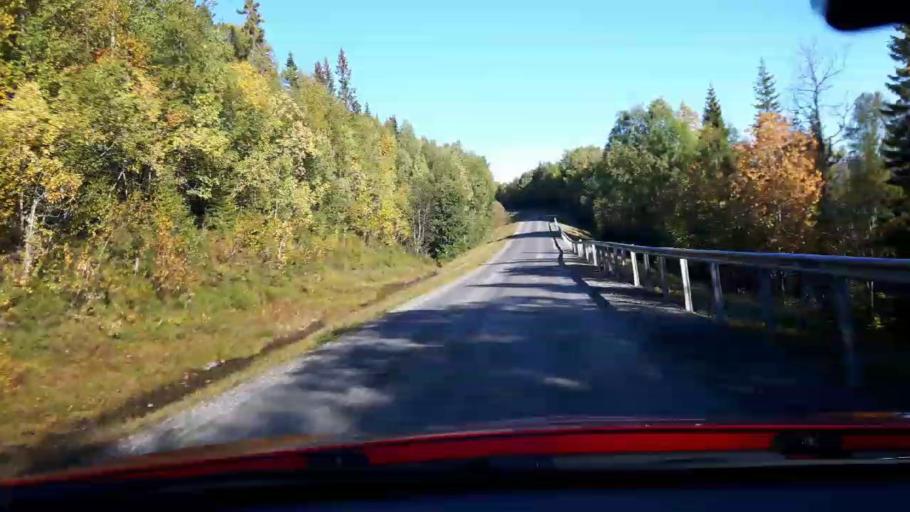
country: NO
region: Nord-Trondelag
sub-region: Lierne
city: Sandvika
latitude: 64.5702
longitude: 13.9034
